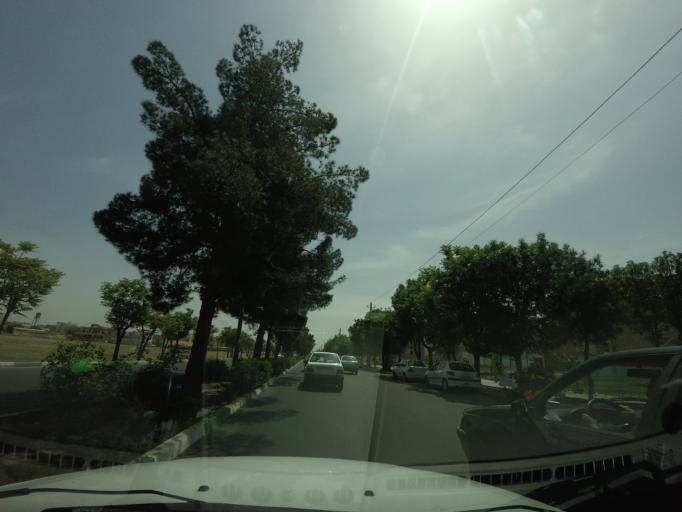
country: IR
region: Tehran
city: Eslamshahr
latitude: 35.5380
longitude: 51.2106
